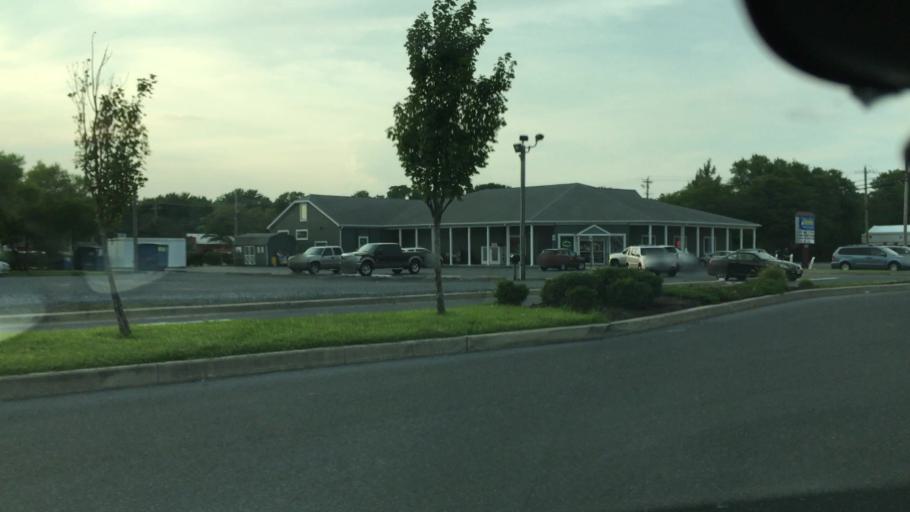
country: US
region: Delaware
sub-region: Sussex County
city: Ocean View
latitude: 38.5465
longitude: -75.1087
